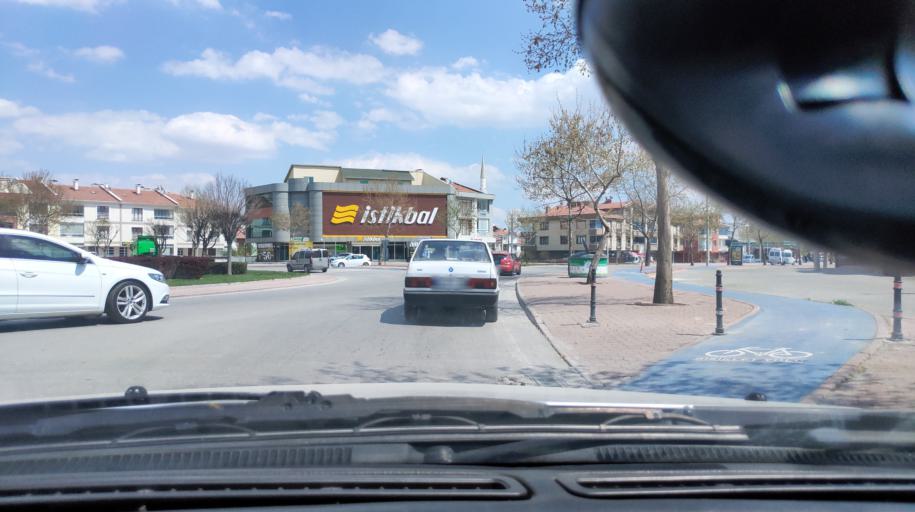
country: TR
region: Konya
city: Selcuklu
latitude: 37.9295
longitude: 32.4930
